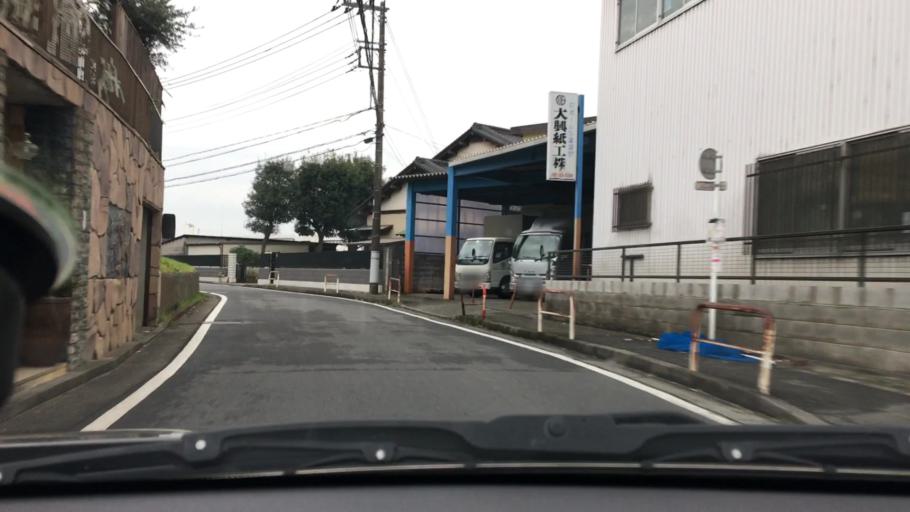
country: JP
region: Kanagawa
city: Yokohama
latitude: 35.5205
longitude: 139.6036
